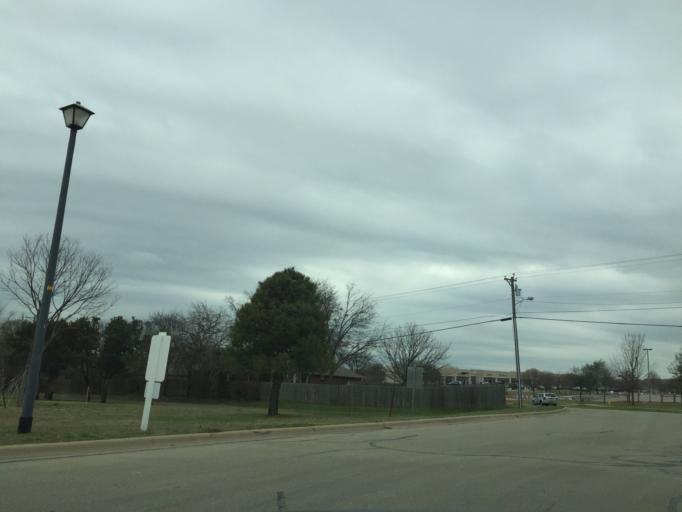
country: US
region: Texas
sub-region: Bell County
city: Harker Heights
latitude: 31.0680
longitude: -97.6639
